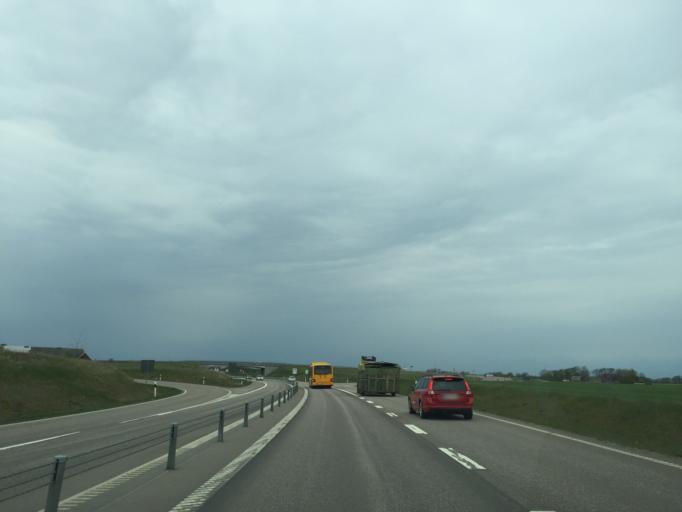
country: SE
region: Skane
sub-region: Hoganas Kommun
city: Hoganas
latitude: 56.1622
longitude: 12.5888
